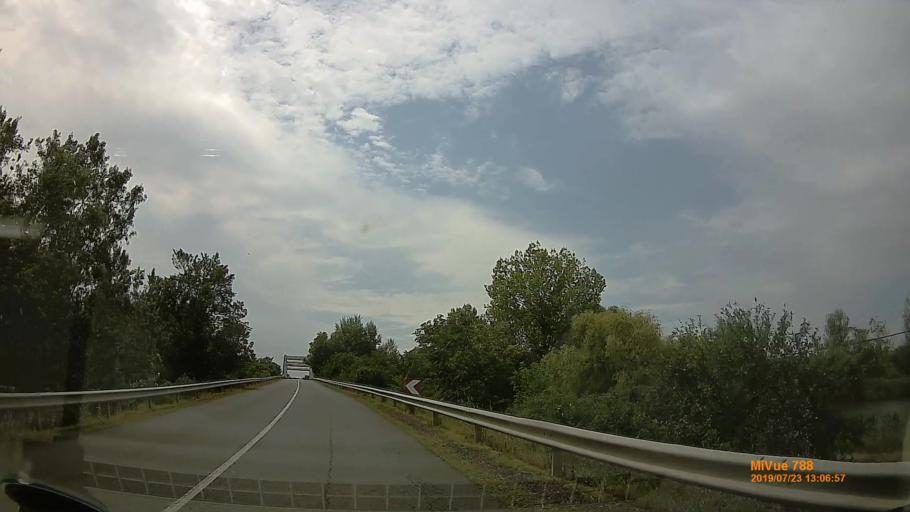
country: HU
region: Szabolcs-Szatmar-Bereg
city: Tiszavasvari
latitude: 47.9609
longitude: 21.3442
